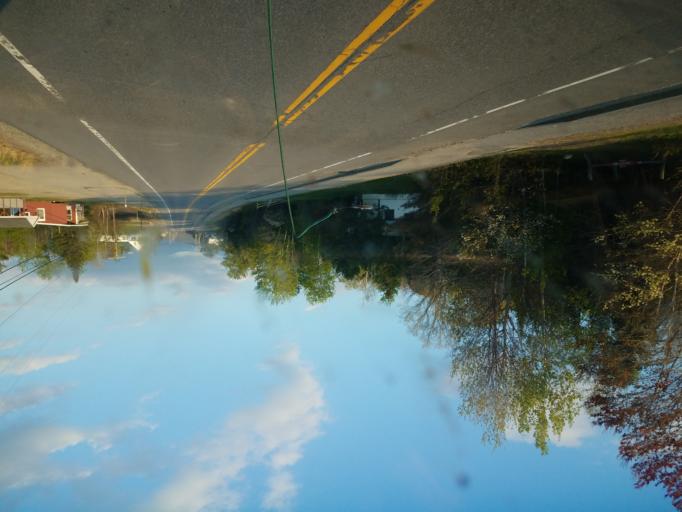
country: US
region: New Hampshire
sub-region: Grafton County
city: Deerfield
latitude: 44.2673
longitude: -71.5563
